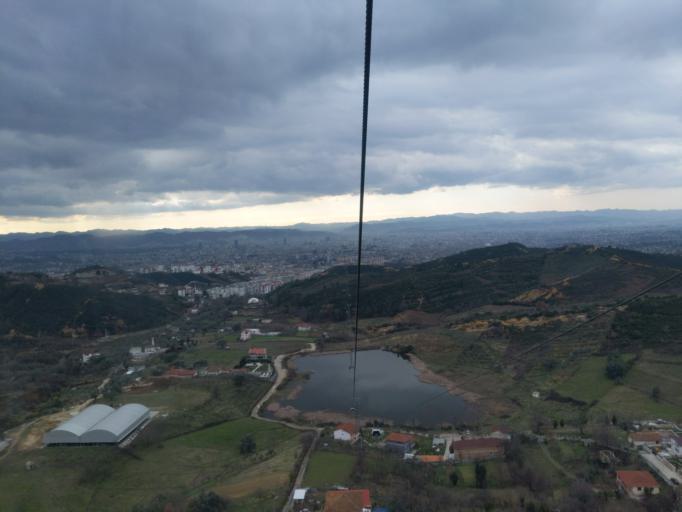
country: AL
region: Tirane
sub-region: Rrethi i Tiranes
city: Dajt
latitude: 41.3588
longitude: 19.8812
